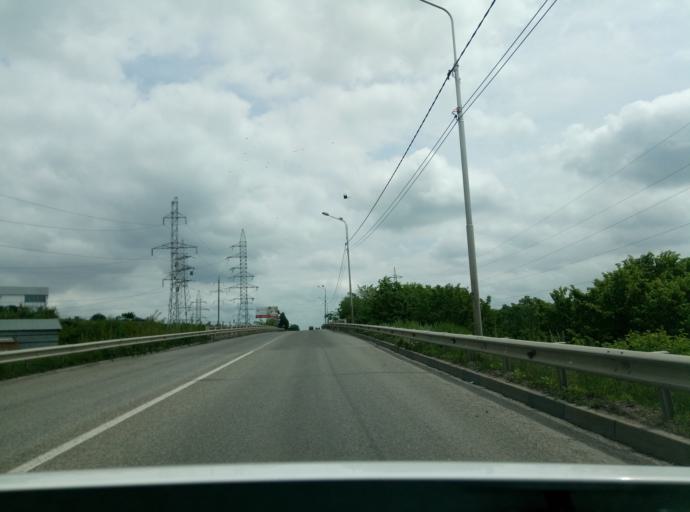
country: RU
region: Stavropol'skiy
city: Pyatigorsk
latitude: 44.0640
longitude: 43.0556
